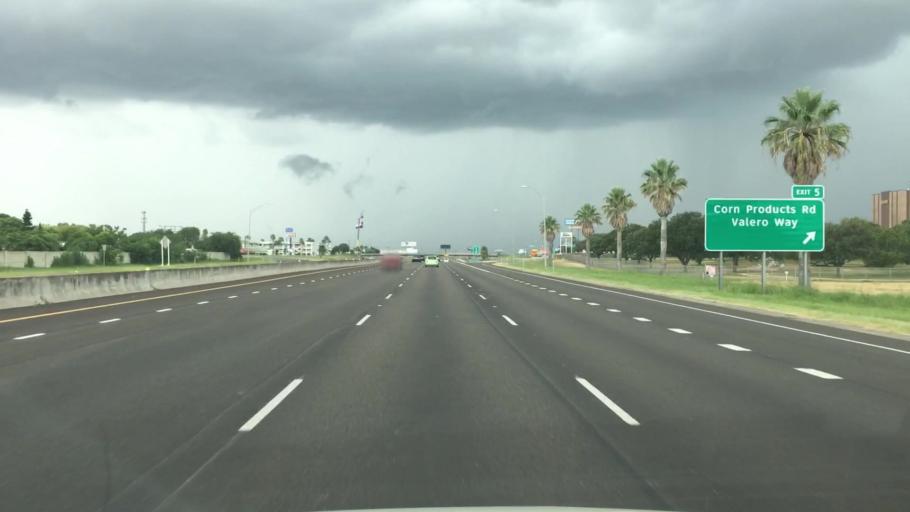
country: US
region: Texas
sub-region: Nueces County
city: Corpus Christi
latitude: 27.8048
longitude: -97.4796
